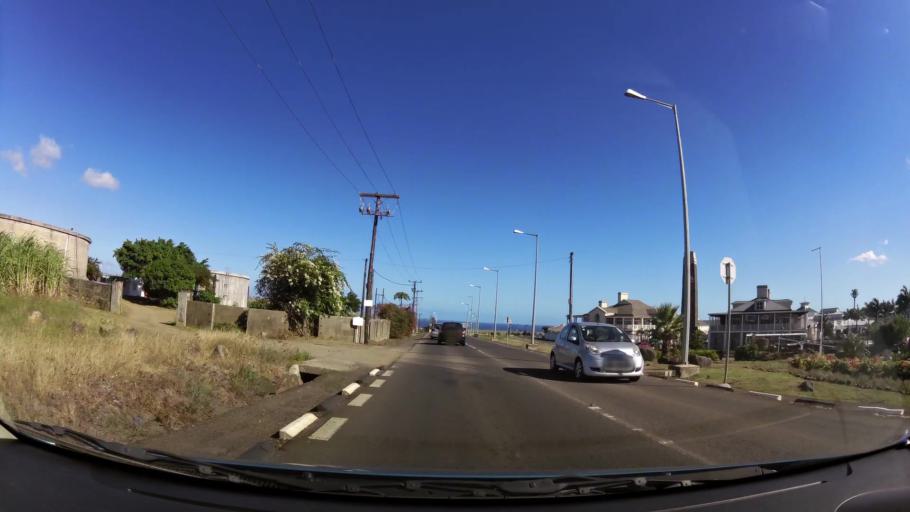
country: MU
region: Black River
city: Cascavelle
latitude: -20.2803
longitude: 57.4034
